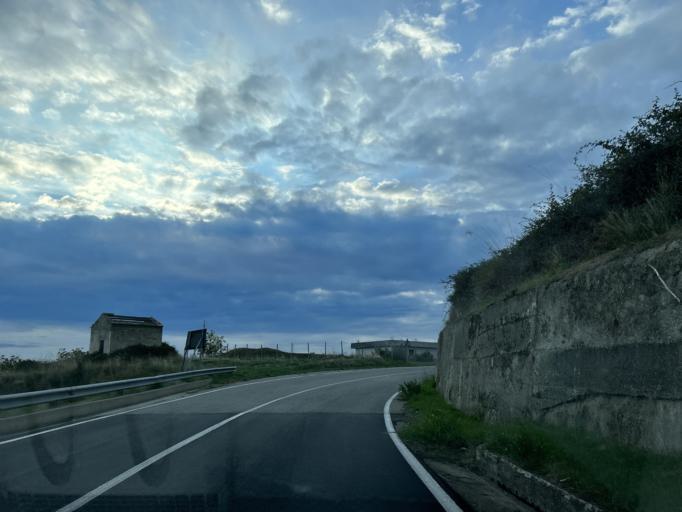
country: IT
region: Calabria
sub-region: Provincia di Catanzaro
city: Montauro
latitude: 38.7564
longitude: 16.5063
